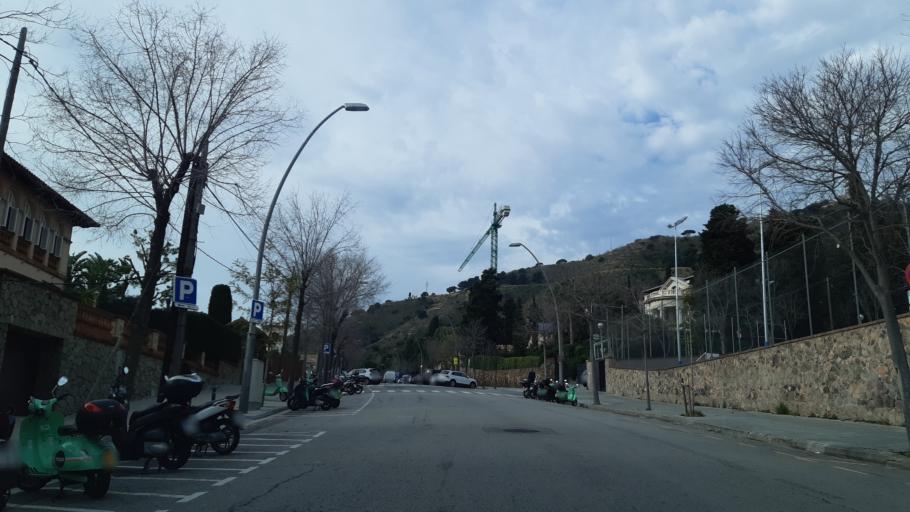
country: ES
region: Catalonia
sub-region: Provincia de Barcelona
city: les Corts
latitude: 41.3936
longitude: 2.1077
